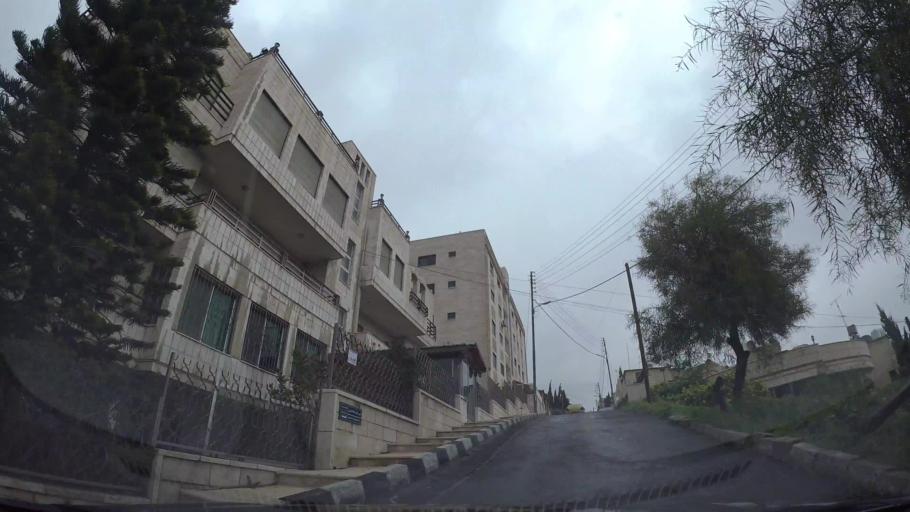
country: JO
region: Amman
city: Amman
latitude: 31.9490
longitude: 35.9099
